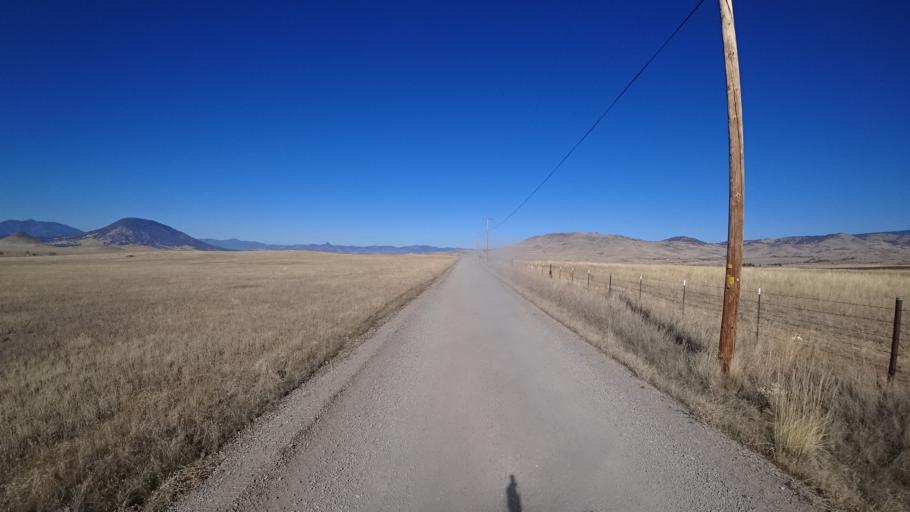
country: US
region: California
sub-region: Siskiyou County
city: Montague
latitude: 41.7989
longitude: -122.4158
